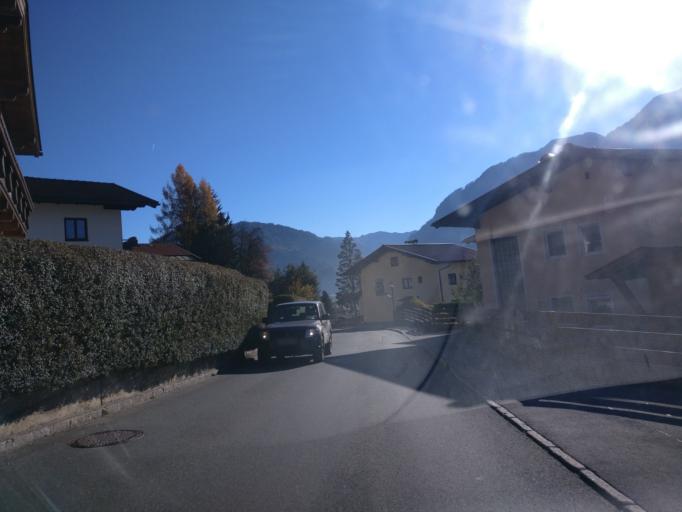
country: AT
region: Salzburg
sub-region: Politischer Bezirk Sankt Johann im Pongau
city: Sankt Veit im Pongau
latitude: 47.3329
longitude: 13.1530
